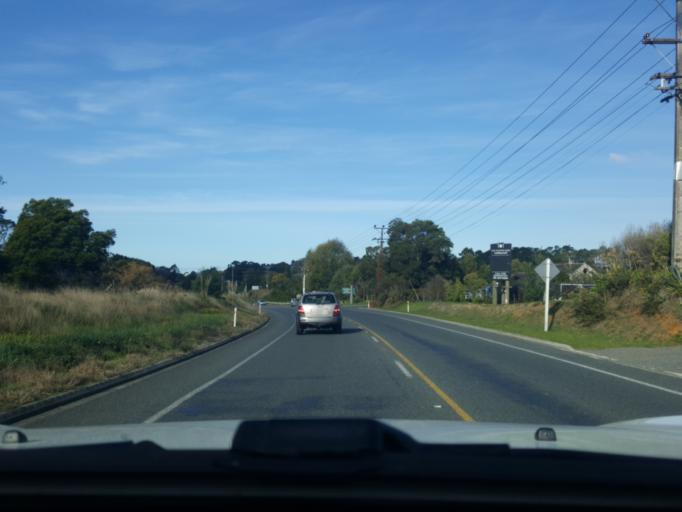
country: NZ
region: Auckland
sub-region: Auckland
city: Muriwai Beach
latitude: -36.7675
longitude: 174.5234
